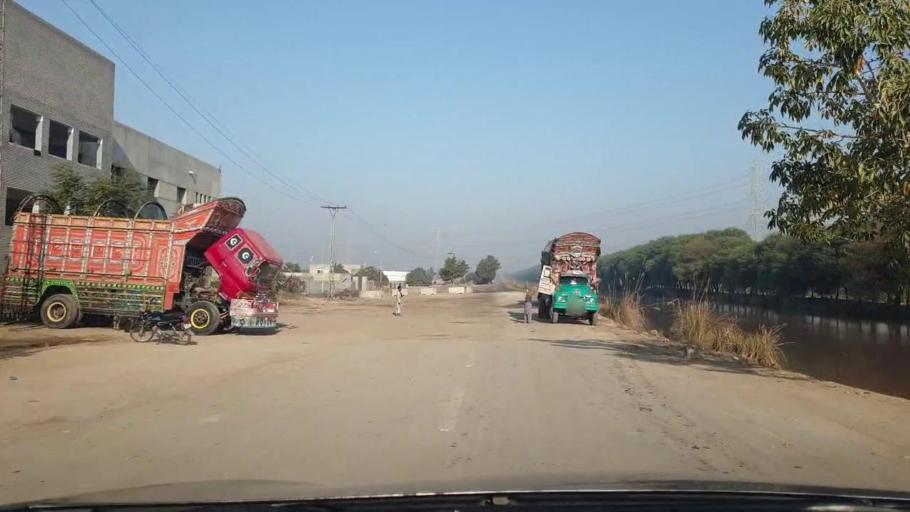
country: PK
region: Sindh
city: Tando Allahyar
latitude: 25.4891
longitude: 68.7164
